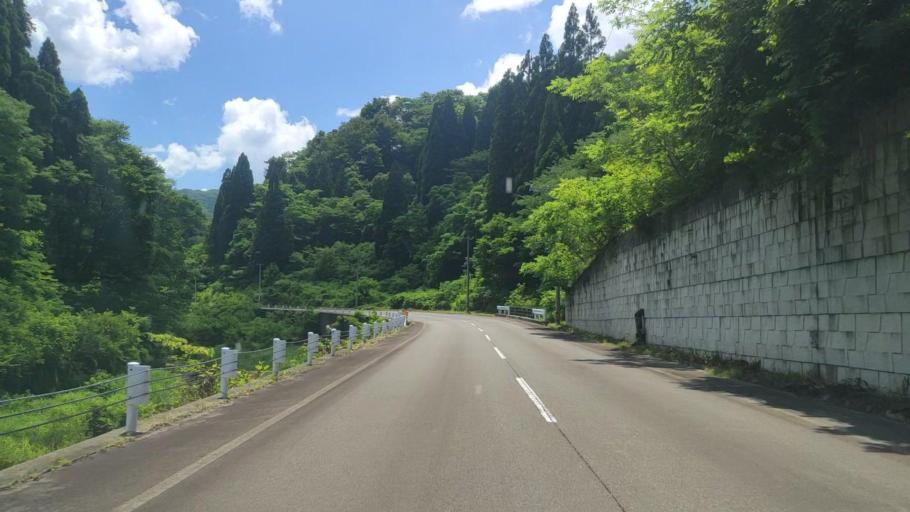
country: JP
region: Fukui
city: Ono
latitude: 35.8364
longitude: 136.4445
